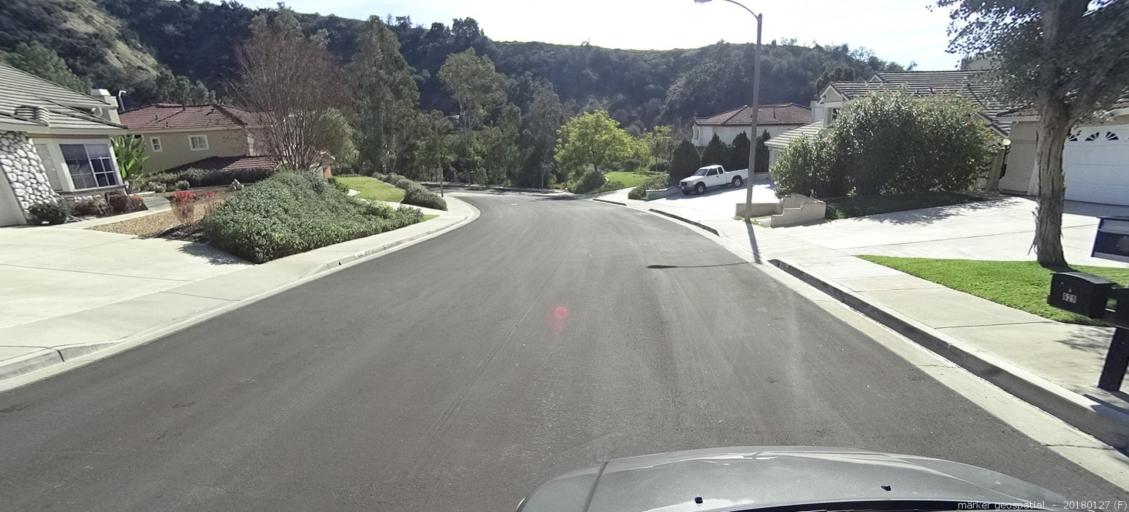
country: US
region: California
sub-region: Los Angeles County
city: Diamond Bar
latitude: 34.0151
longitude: -117.8036
